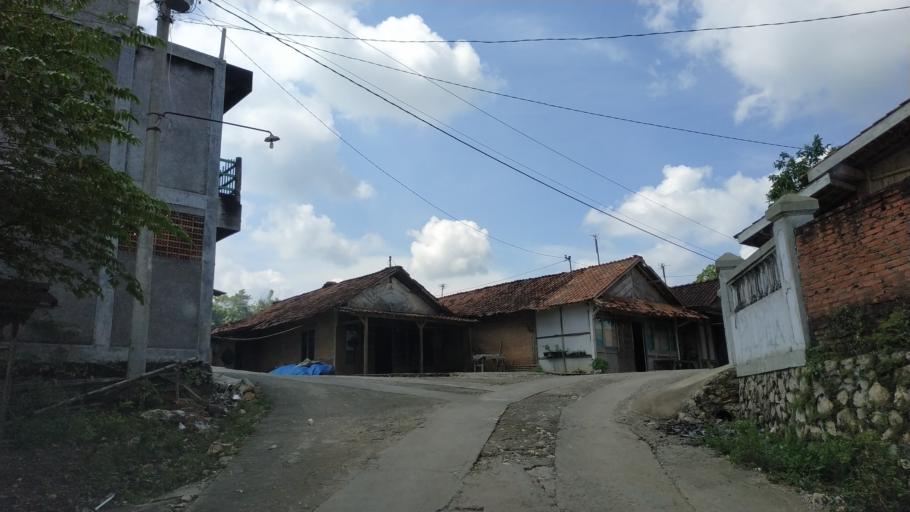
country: ID
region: Central Java
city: Guyangan
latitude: -7.0052
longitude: 111.1084
